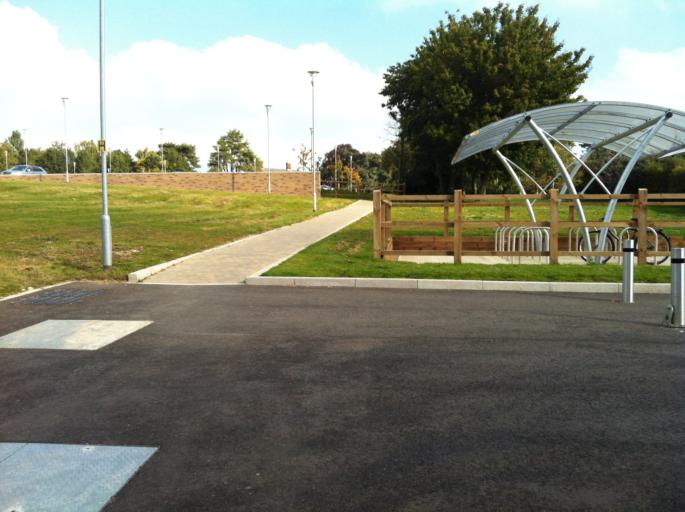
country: GB
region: England
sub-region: Norfolk
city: Bowthorpe
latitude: 52.6231
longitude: 1.2196
